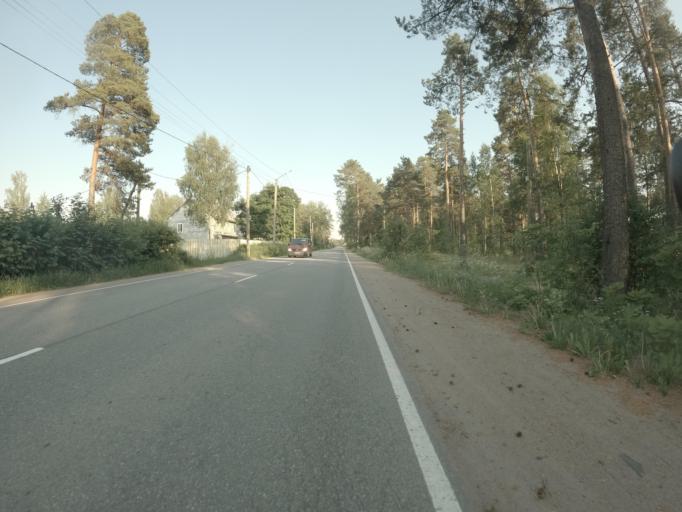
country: RU
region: Leningrad
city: Yakovlevo
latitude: 60.4720
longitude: 29.2815
